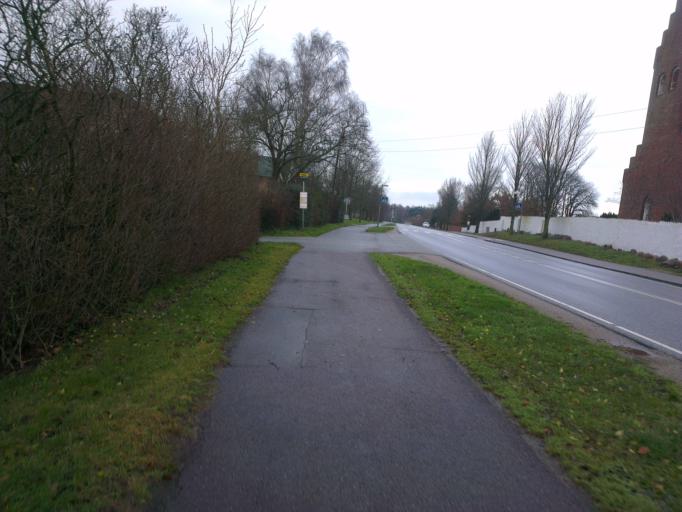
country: DK
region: Capital Region
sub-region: Frederikssund Kommune
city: Jaegerspris
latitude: 55.8404
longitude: 11.9881
